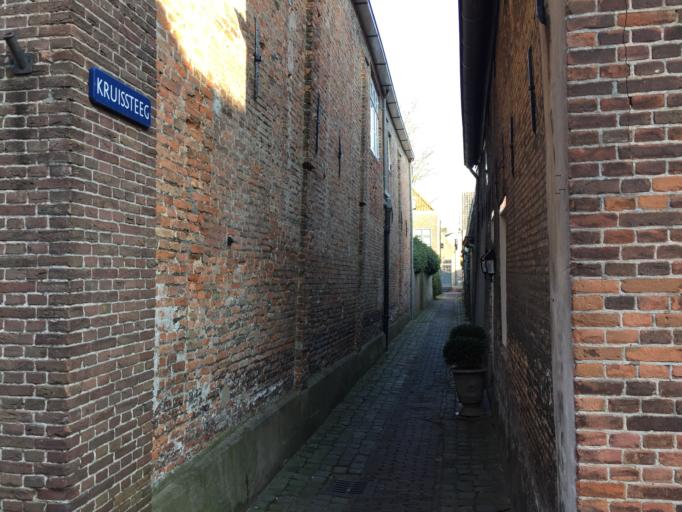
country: NL
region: South Holland
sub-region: Gemeente Schoonhoven
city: Schoonhoven
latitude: 51.9475
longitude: 4.8506
